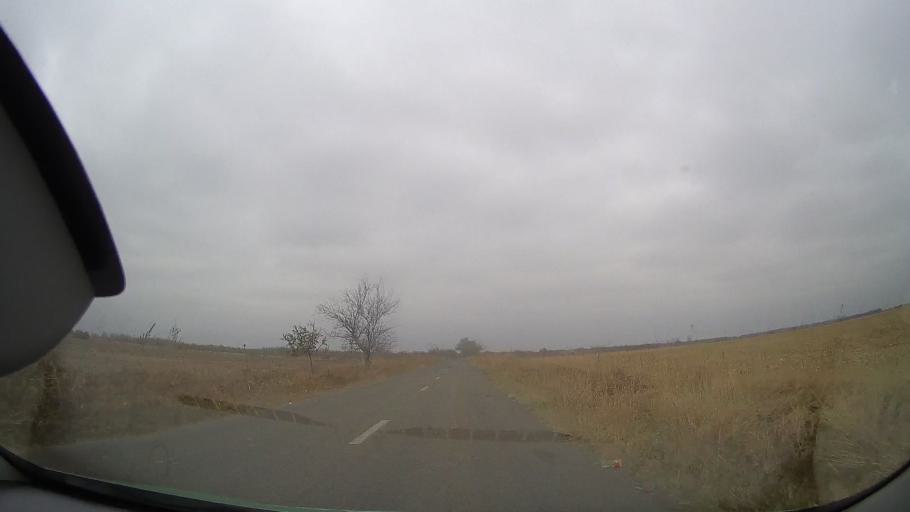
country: RO
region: Buzau
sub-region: Comuna Bradeanu
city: Bradeanu
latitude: 44.9122
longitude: 26.8694
